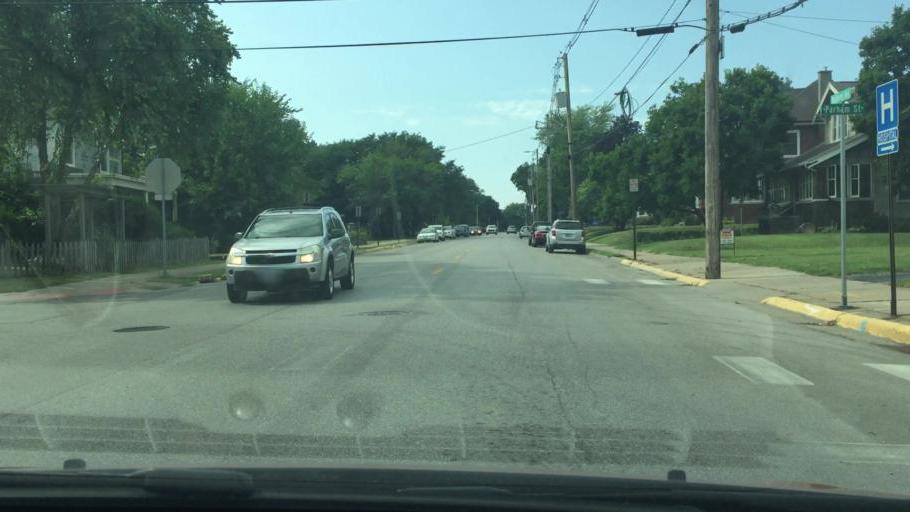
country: US
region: Iowa
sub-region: Muscatine County
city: Muscatine
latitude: 41.4355
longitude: -91.0541
